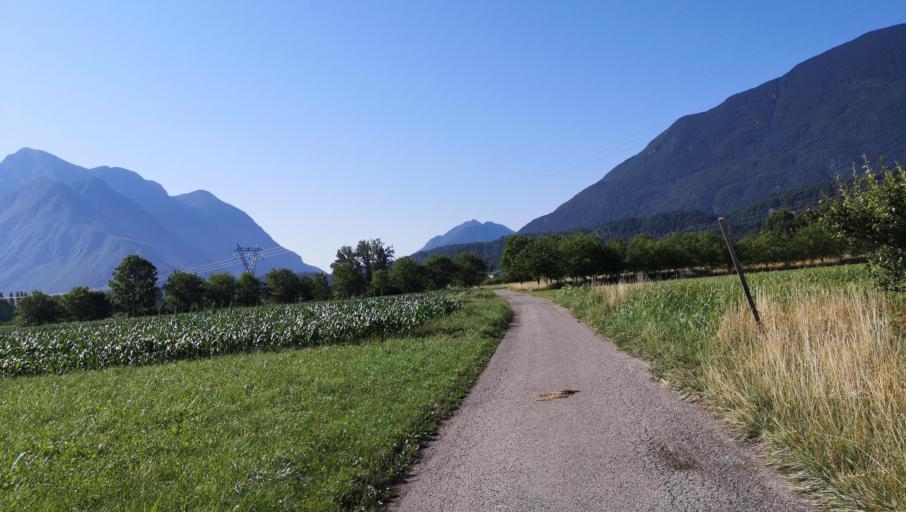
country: IT
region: Friuli Venezia Giulia
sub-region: Provincia di Udine
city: Cavazzo Carnico
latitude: 46.3757
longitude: 13.0416
